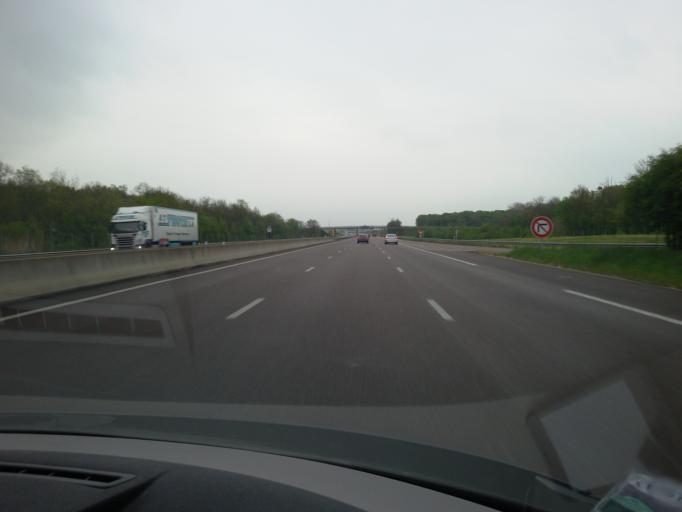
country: FR
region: Bourgogne
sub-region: Departement de la Cote-d'Or
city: Perrigny-les-Dijon
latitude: 47.2249
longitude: 5.0113
